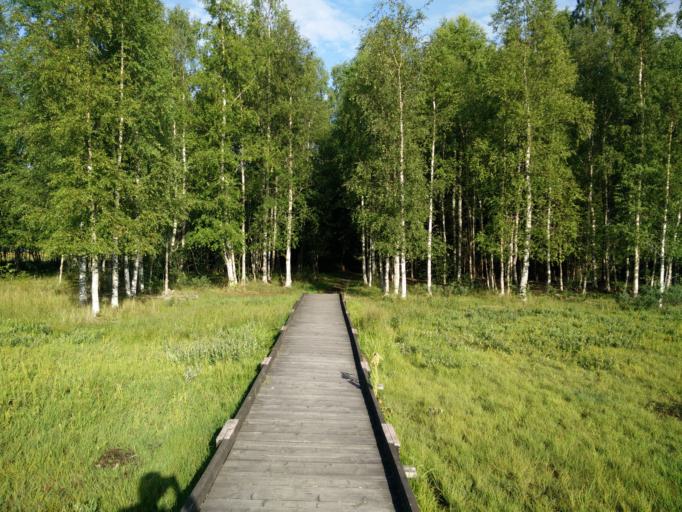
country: SE
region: Vaesternorrland
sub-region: Timra Kommun
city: Soraker
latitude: 62.4502
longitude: 17.4927
